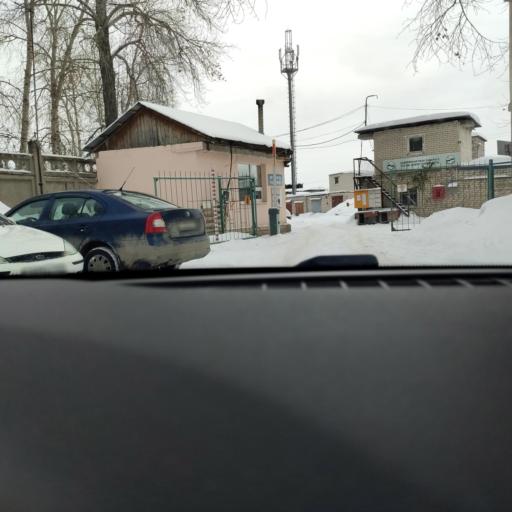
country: RU
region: Samara
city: Samara
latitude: 53.1792
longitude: 50.1145
